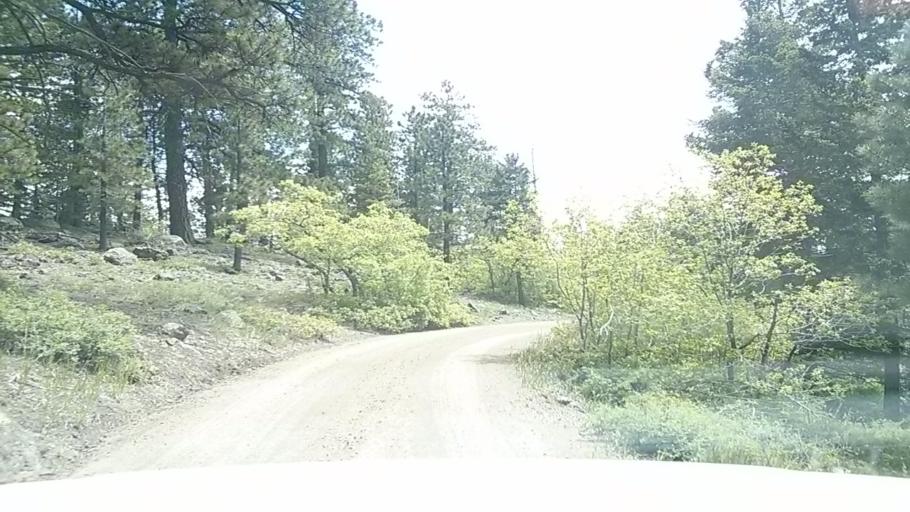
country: US
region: Utah
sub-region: Wayne County
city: Loa
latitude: 37.9377
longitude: -111.6949
